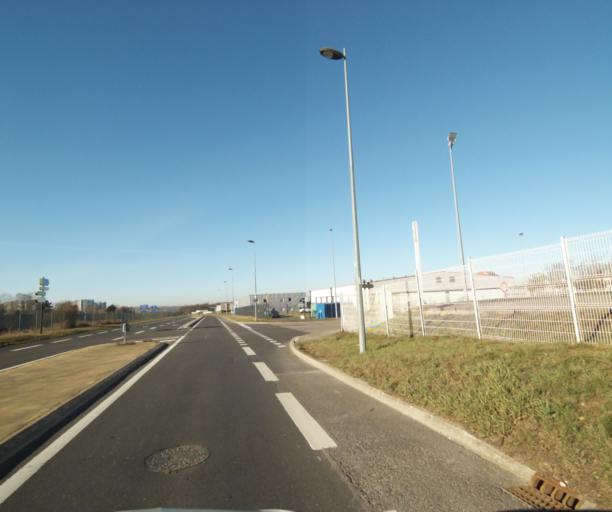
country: FR
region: Lorraine
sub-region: Departement de Meurthe-et-Moselle
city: Laxou
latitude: 48.7024
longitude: 6.1277
